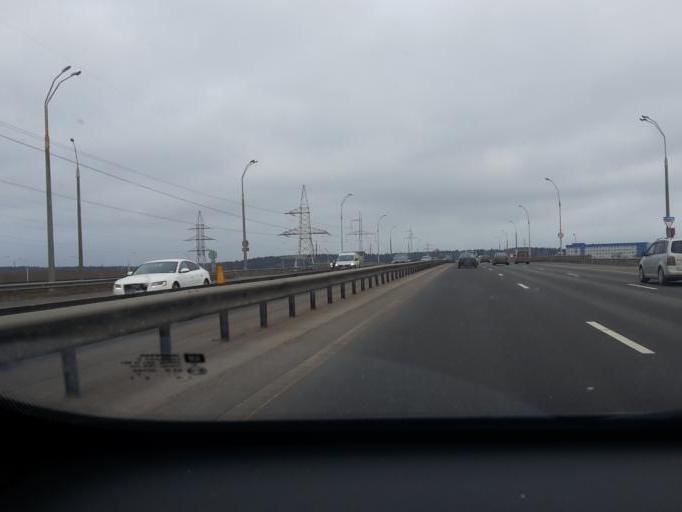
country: BY
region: Minsk
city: Novoye Medvezhino
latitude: 53.8937
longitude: 27.4111
